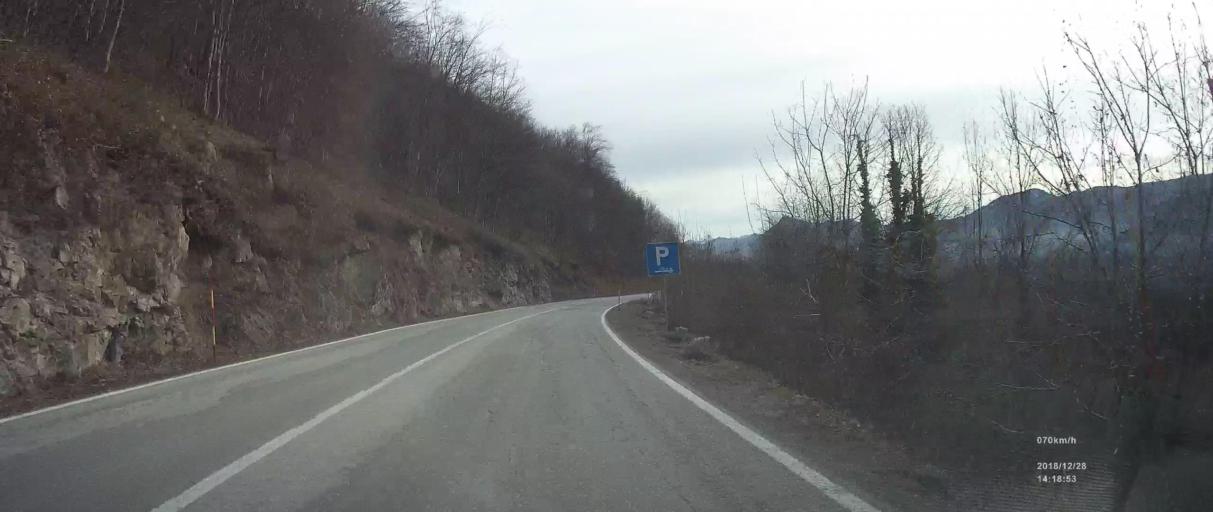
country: HR
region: Primorsko-Goranska
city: Vrbovsko
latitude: 45.4086
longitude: 15.0620
